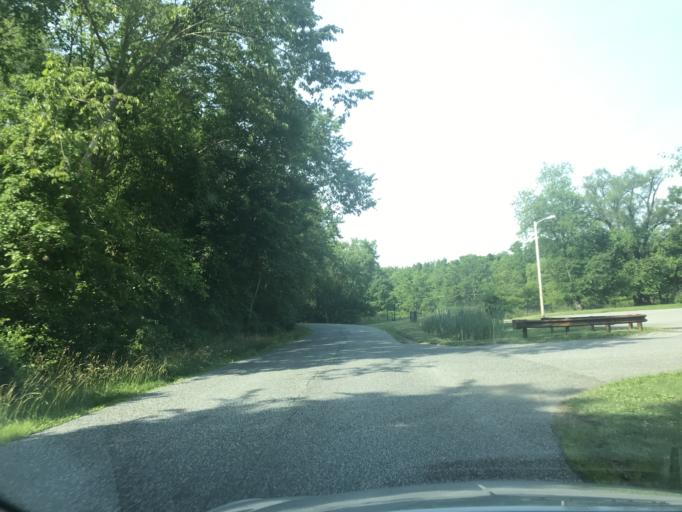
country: US
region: Maryland
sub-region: Harford County
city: Bel Air North
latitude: 39.5690
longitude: -76.3652
